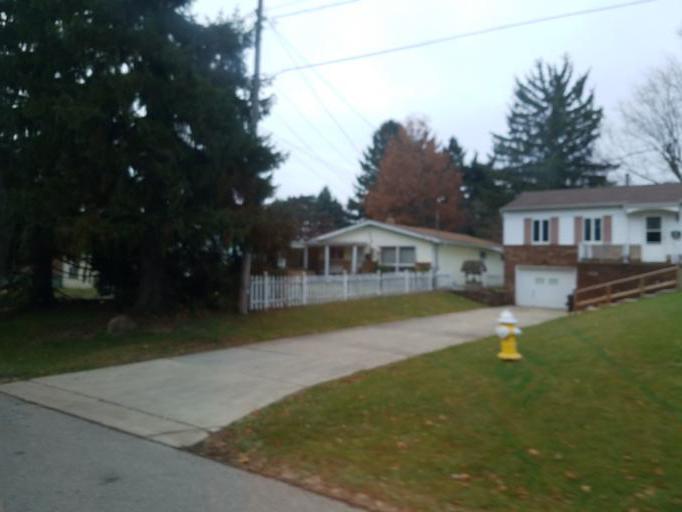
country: US
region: Ohio
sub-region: Richland County
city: Mansfield
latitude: 40.7445
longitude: -82.5086
